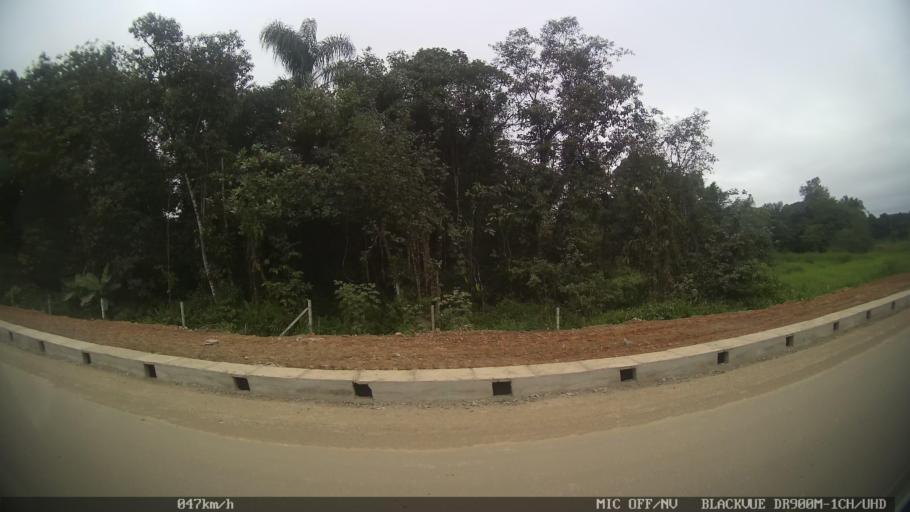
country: BR
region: Santa Catarina
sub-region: Joinville
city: Joinville
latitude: -26.2503
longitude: -48.8618
